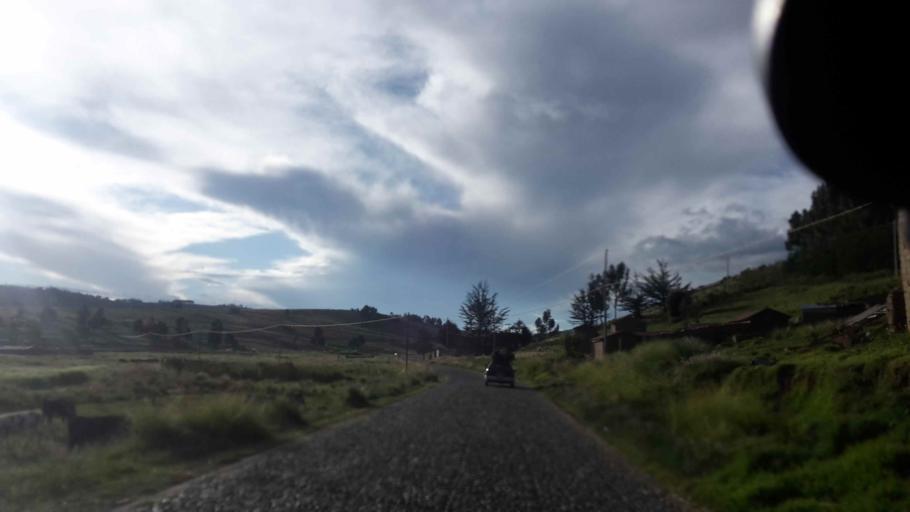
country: BO
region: Cochabamba
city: Arani
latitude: -17.5332
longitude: -65.6553
